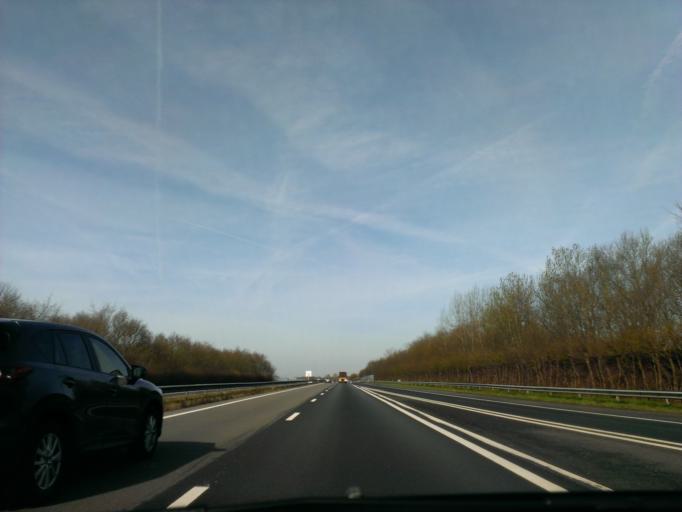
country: NL
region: Gelderland
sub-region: Gemeente Harderwijk
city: Harderwijk
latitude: 52.3305
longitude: 5.6151
